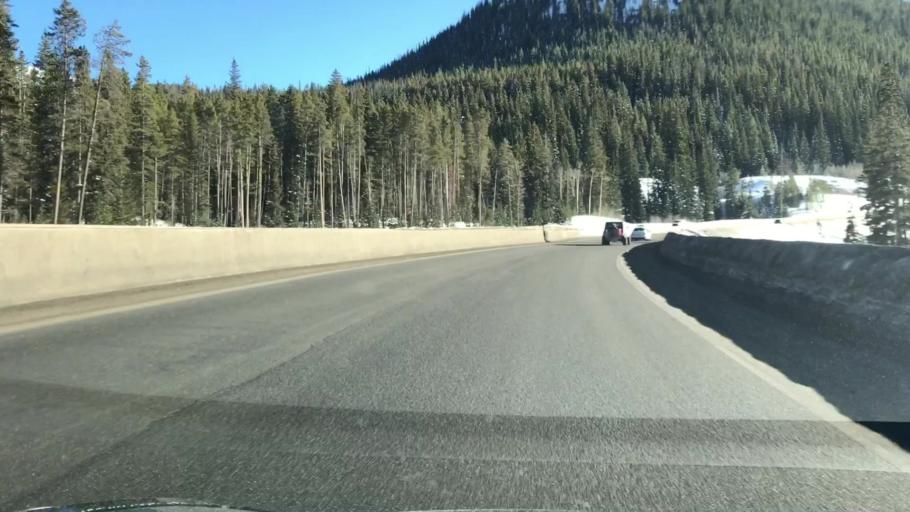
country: US
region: Colorado
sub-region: Eagle County
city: Vail
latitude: 39.5914
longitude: -106.2467
